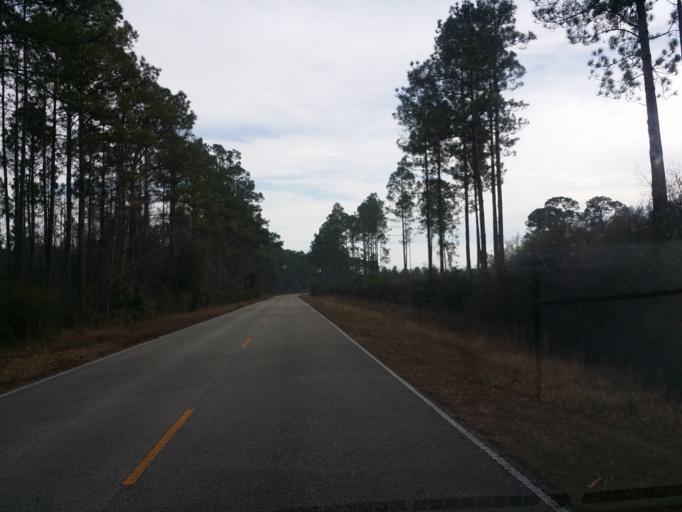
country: US
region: Florida
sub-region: Leon County
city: Woodville
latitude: 30.1793
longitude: -84.1633
